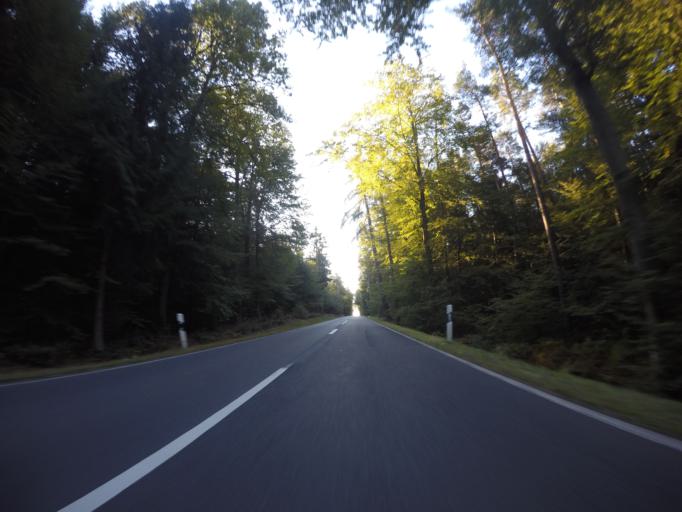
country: DE
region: Bavaria
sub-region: Regierungsbezirk Unterfranken
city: Schollbrunn
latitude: 49.8449
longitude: 9.4481
